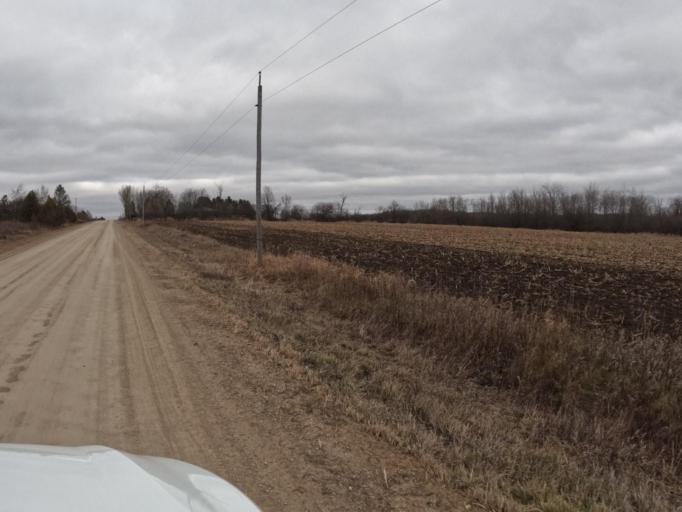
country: CA
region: Ontario
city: Shelburne
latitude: 43.9381
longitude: -80.3940
